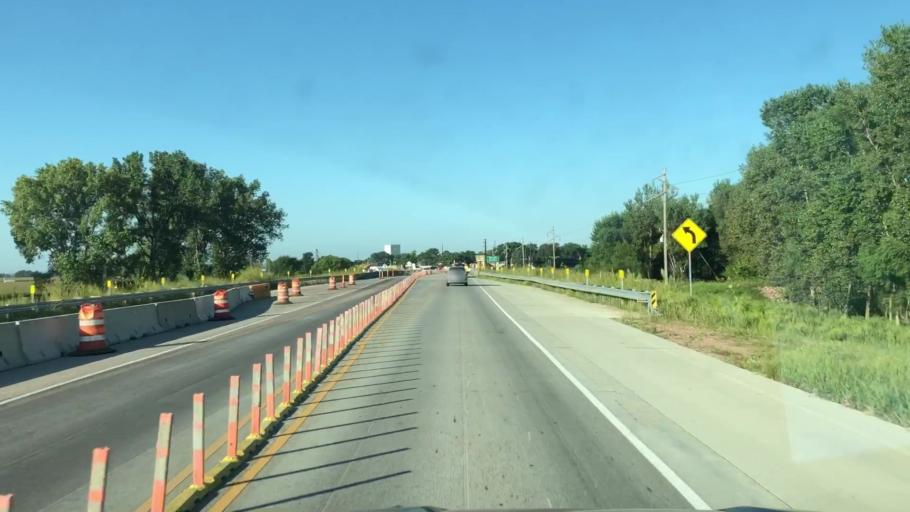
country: US
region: Iowa
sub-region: Plymouth County
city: Le Mars
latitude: 42.7253
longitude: -96.2401
